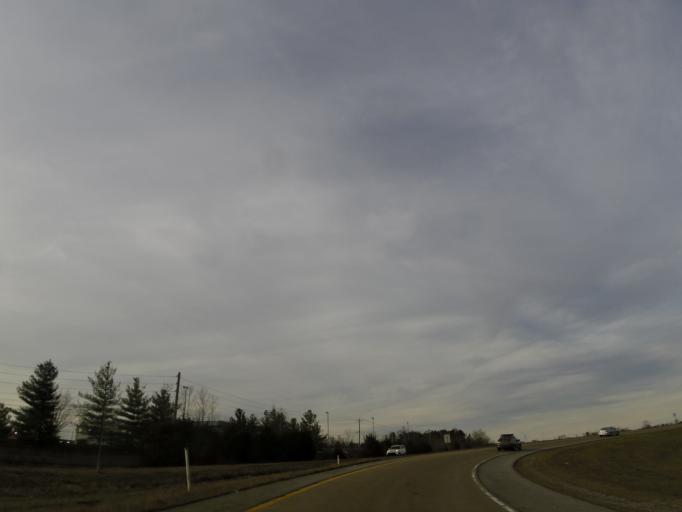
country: US
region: Tennessee
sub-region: Knox County
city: Farragut
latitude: 35.9117
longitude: -84.1246
